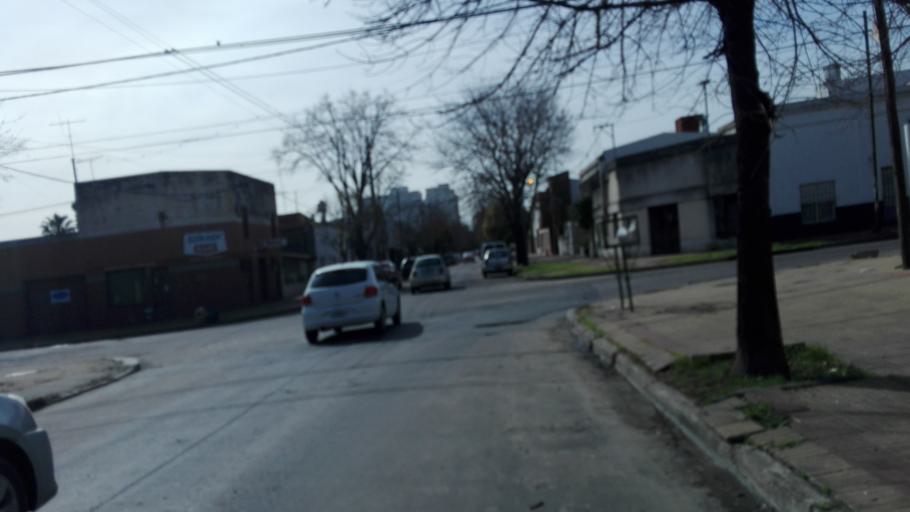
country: AR
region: Buenos Aires
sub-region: Partido de La Plata
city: La Plata
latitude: -34.9126
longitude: -57.9738
